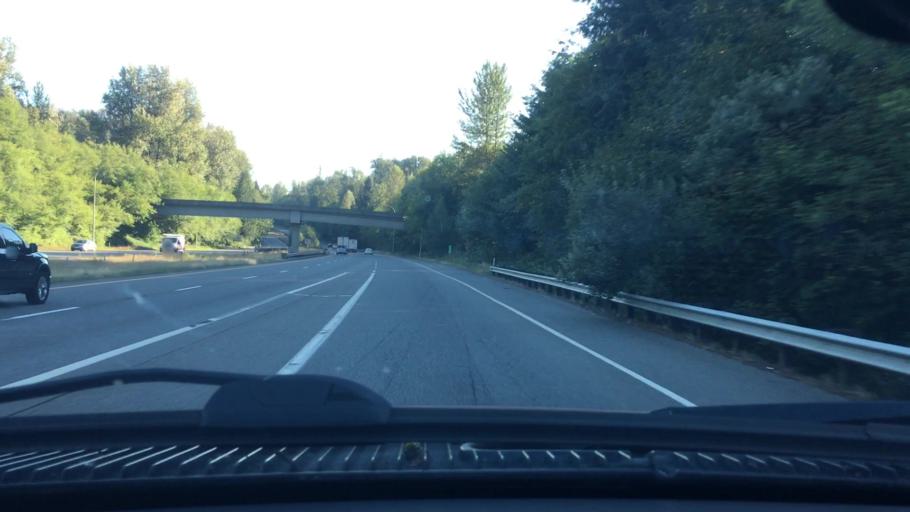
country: US
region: Washington
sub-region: King County
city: Hobart
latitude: 47.4337
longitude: -121.9814
